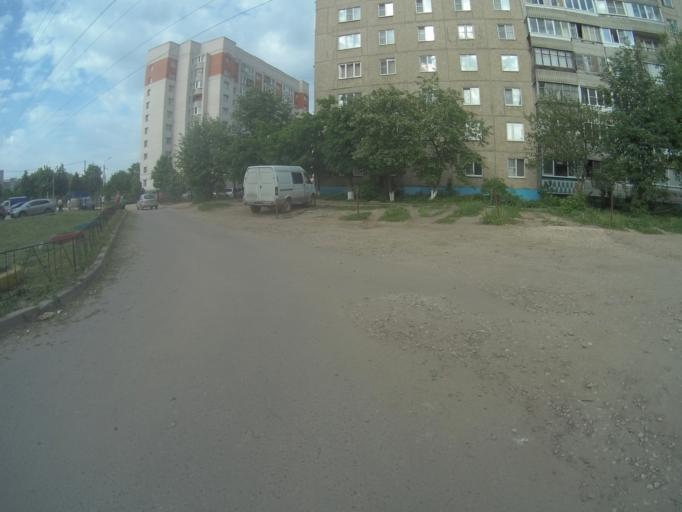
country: RU
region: Vladimir
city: Kommunar
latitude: 56.1640
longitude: 40.4515
